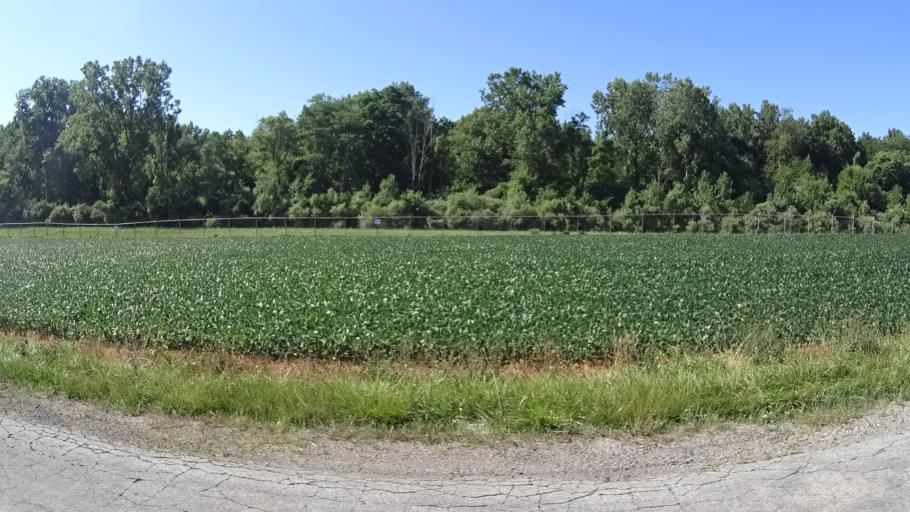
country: US
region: Ohio
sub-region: Erie County
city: Sandusky
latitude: 41.3794
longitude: -82.7095
